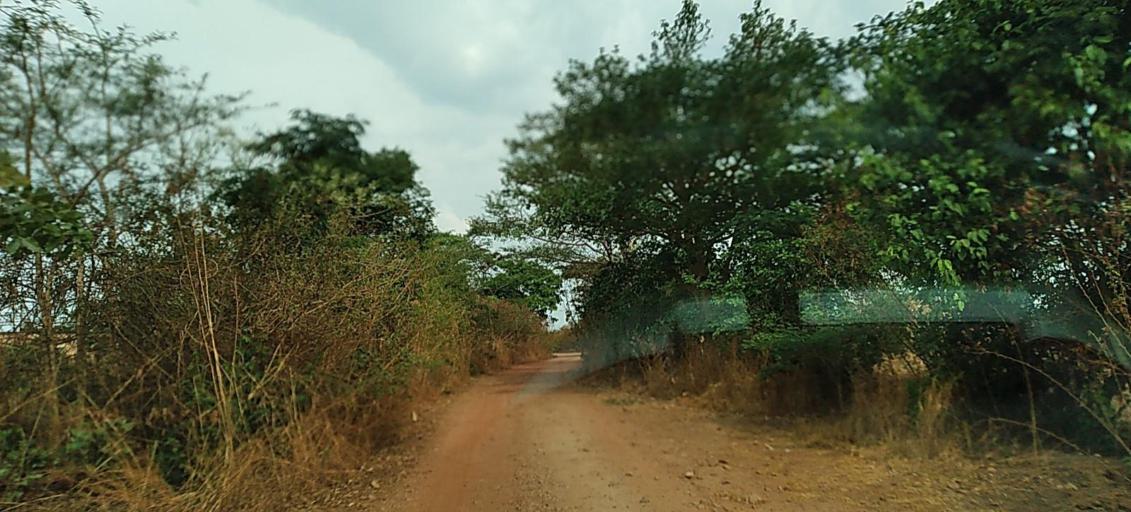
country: ZM
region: Copperbelt
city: Chililabombwe
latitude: -12.3938
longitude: 27.8043
